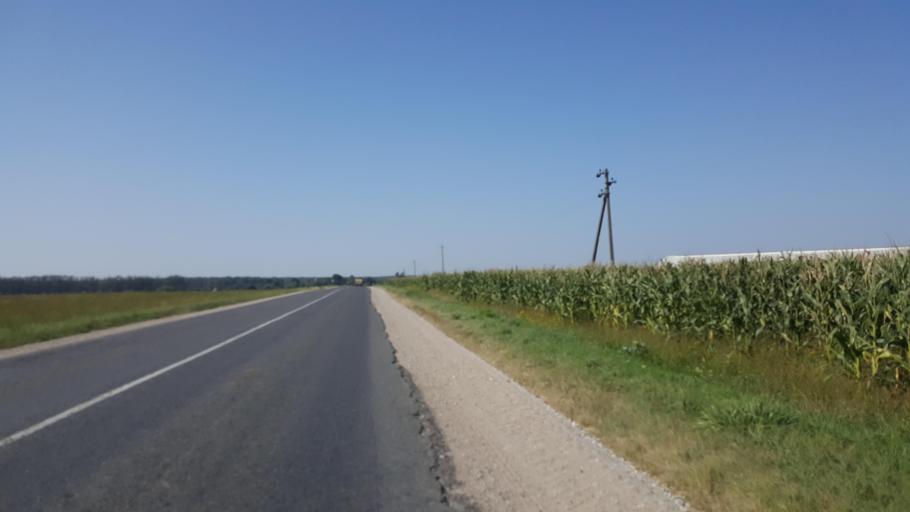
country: BY
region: Brest
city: Kamyanyets
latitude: 52.4141
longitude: 23.6094
